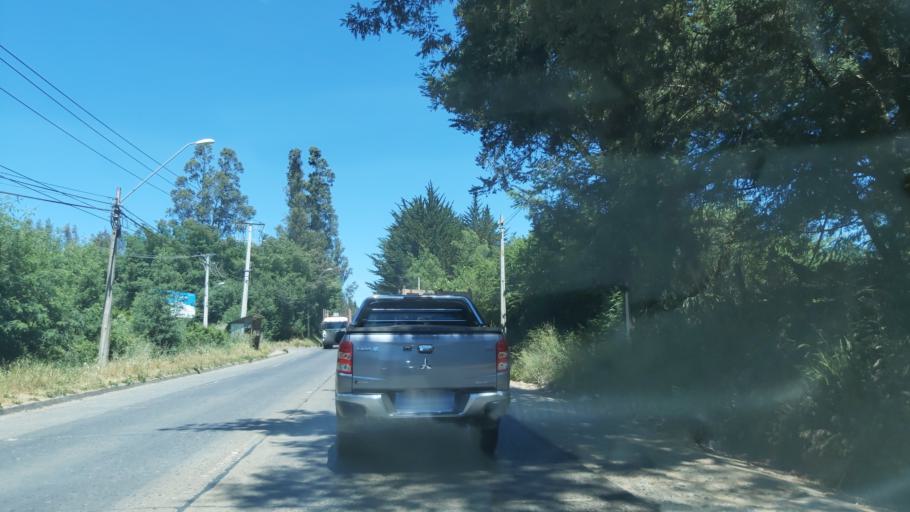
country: CL
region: Maule
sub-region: Provincia de Talca
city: Constitucion
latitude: -35.3560
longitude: -72.4088
